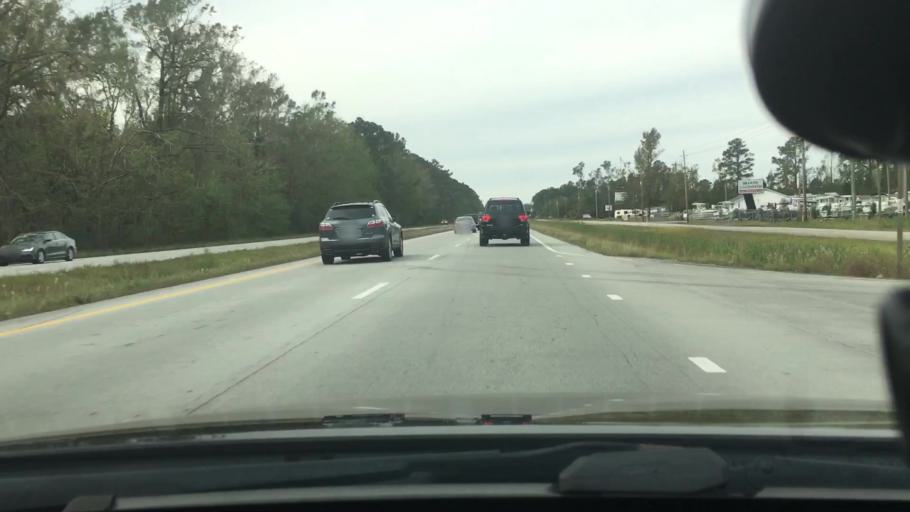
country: US
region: North Carolina
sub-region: Craven County
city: Fairfield Harbour
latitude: 35.0277
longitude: -77.0015
